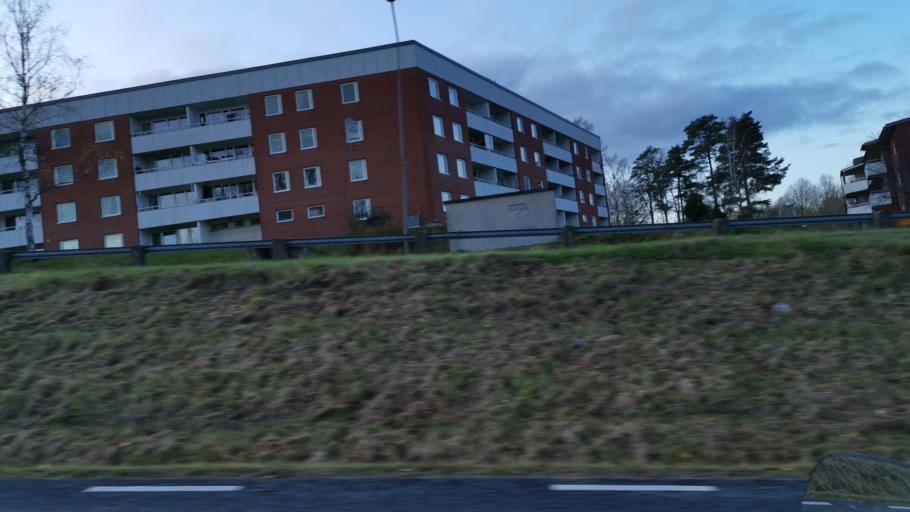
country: SE
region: Vaestra Goetaland
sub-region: Munkedals Kommun
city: Munkedal
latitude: 58.4609
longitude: 11.6752
